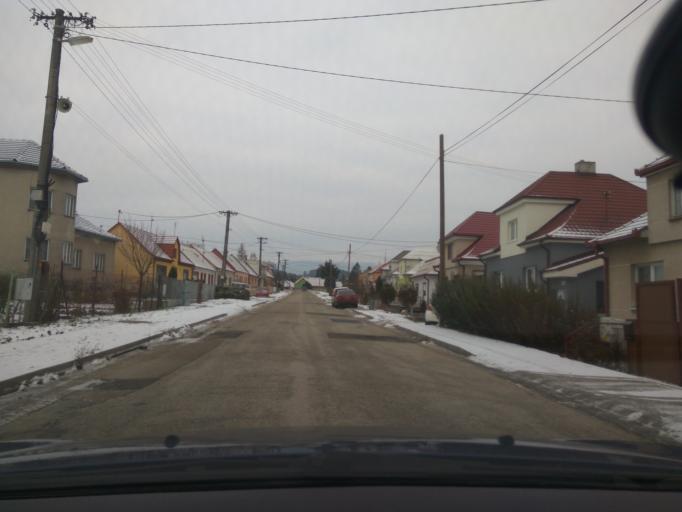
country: SK
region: Nitriansky
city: Stara Tura
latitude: 48.7786
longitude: 17.7400
